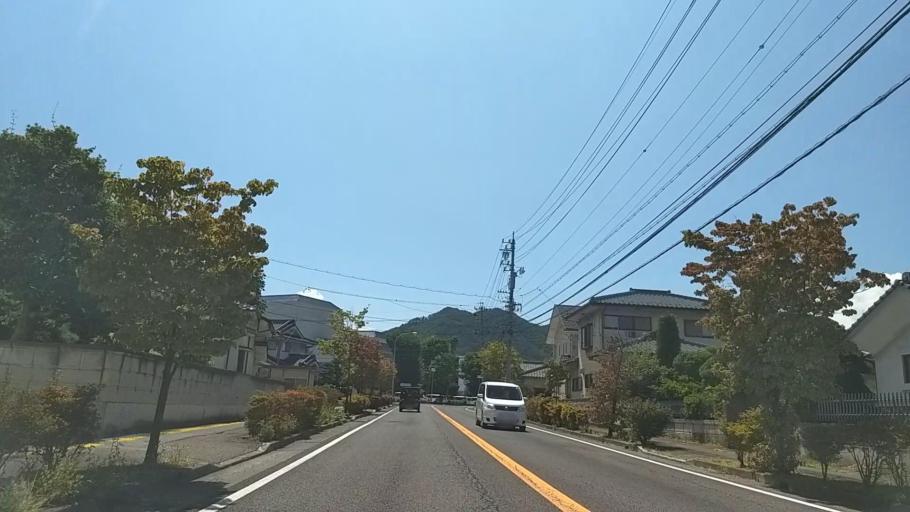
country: JP
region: Nagano
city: Kamimaruko
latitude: 36.3201
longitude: 138.2695
